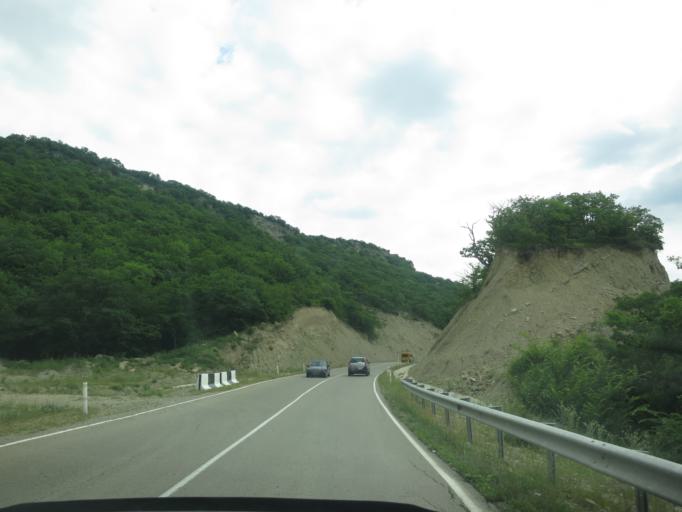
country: GE
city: Didi Lilo
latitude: 41.8092
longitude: 45.1422
